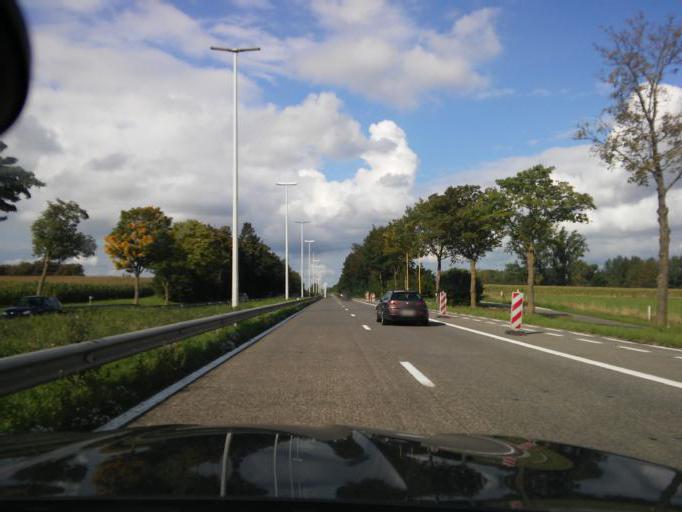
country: BE
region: Flanders
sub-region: Provincie Oost-Vlaanderen
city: Haaltert
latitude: 50.8818
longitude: 4.0317
